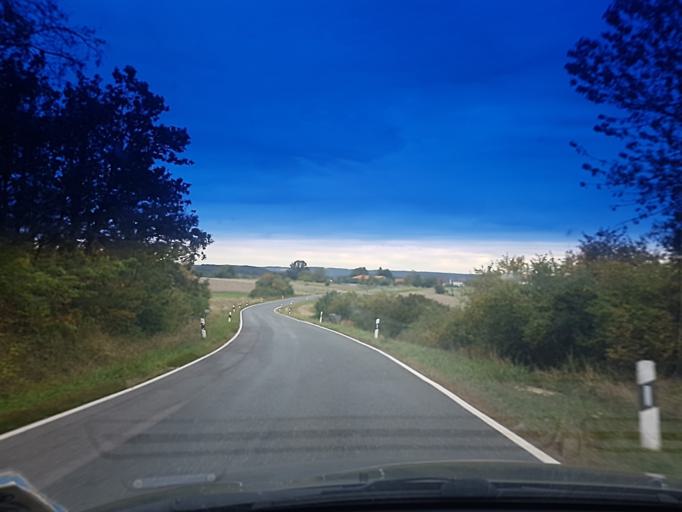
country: DE
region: Bavaria
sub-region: Regierungsbezirk Unterfranken
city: Geiselwind
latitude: 49.8036
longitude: 10.4864
